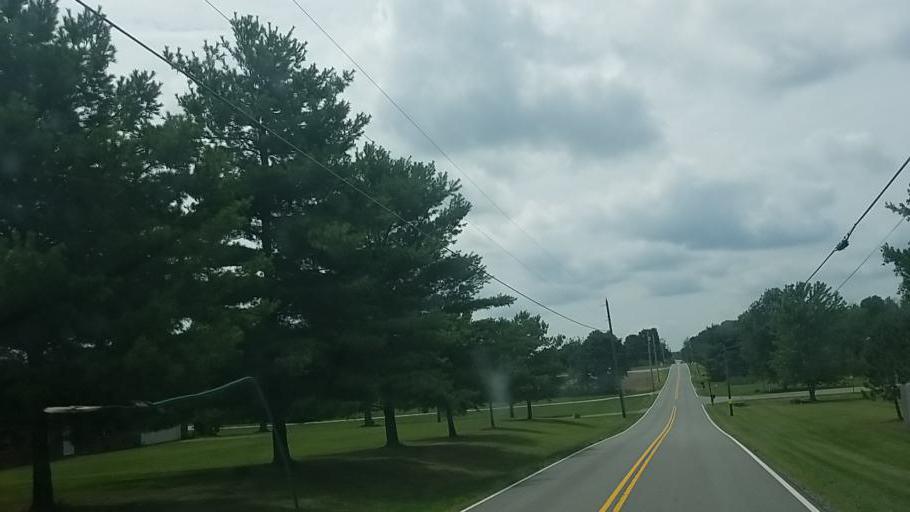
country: US
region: Ohio
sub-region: Fairfield County
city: Lithopolis
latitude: 39.7509
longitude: -82.8179
